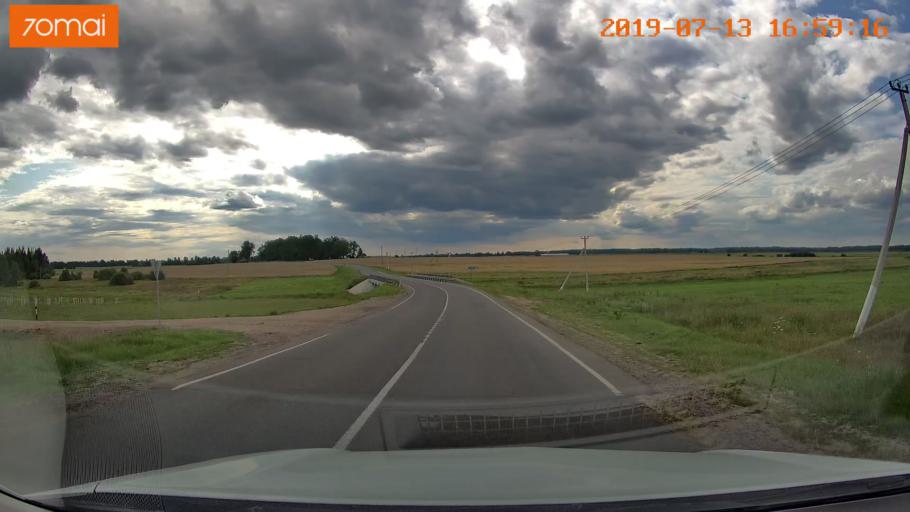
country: BY
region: Mogilev
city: Kirawsk
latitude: 53.2977
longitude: 29.4325
